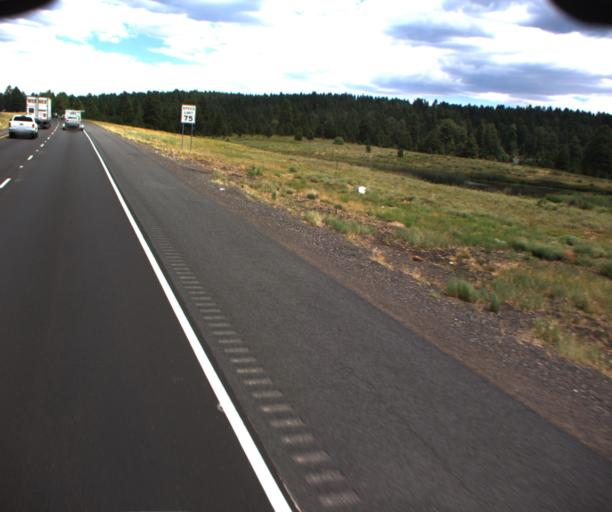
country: US
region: Arizona
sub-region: Coconino County
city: Kachina Village
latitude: 35.1015
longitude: -111.6819
